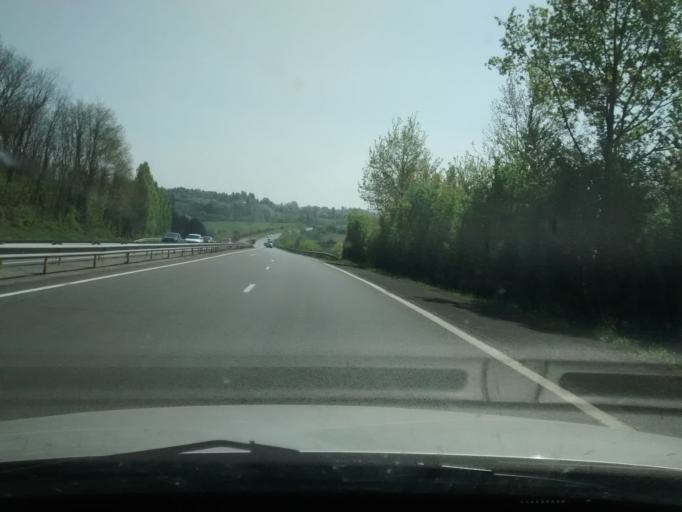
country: FR
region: Pays de la Loire
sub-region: Departement de la Sarthe
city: Coulaines
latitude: 48.0286
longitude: 0.2185
